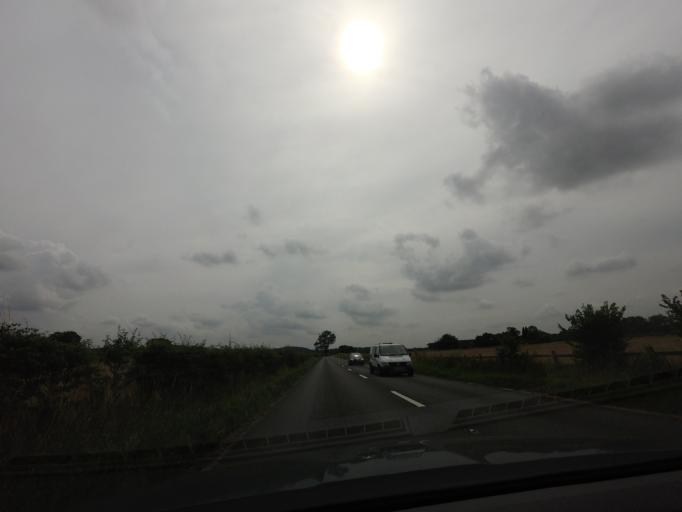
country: GB
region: England
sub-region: Shropshire
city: Tong
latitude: 52.6907
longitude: -2.3157
